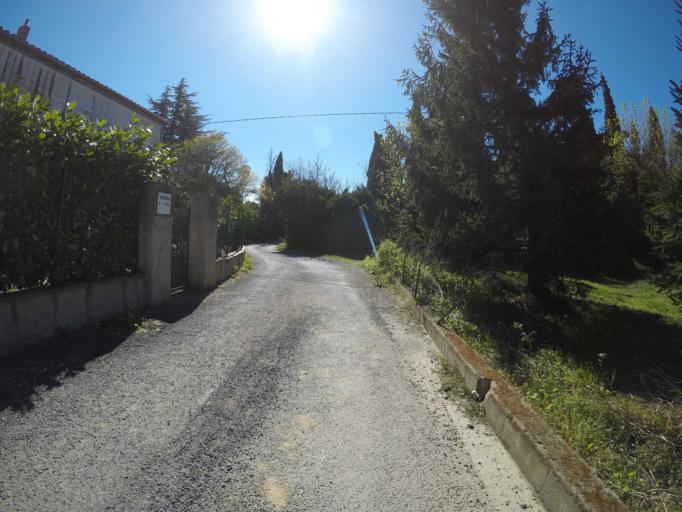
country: FR
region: Languedoc-Roussillon
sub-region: Departement des Pyrenees-Orientales
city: Ille-sur-Tet
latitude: 42.6849
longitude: 2.6548
